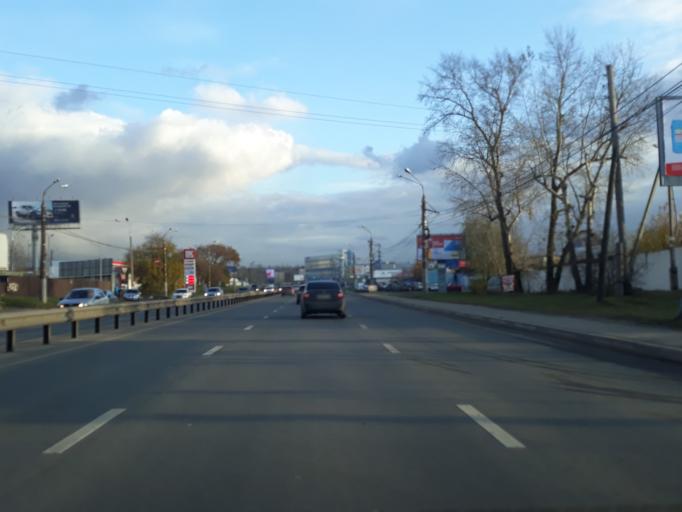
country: RU
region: Nizjnij Novgorod
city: Nizhniy Novgorod
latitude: 56.2994
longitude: 43.9248
